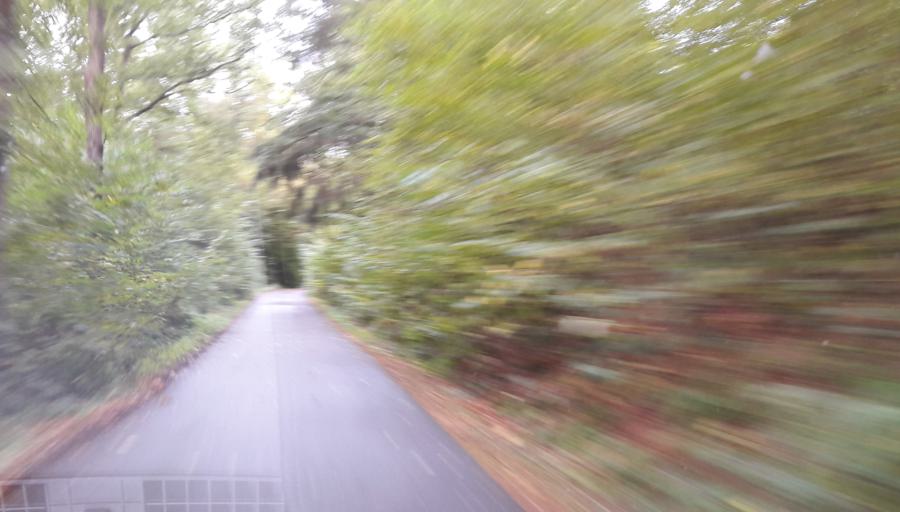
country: DE
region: Rheinland-Pfalz
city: Breitenbach
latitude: 49.4415
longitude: 7.2287
